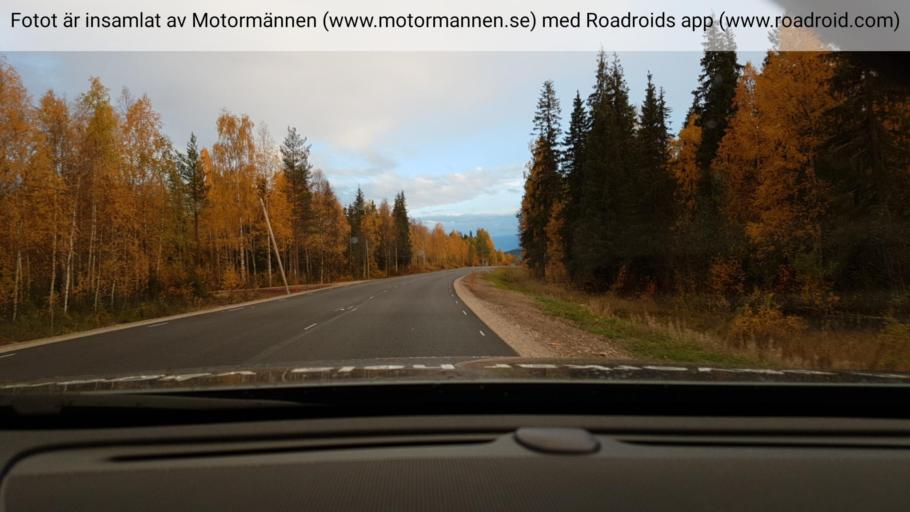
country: SE
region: Norrbotten
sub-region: Overkalix Kommun
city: OEverkalix
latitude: 66.3735
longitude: 22.8419
